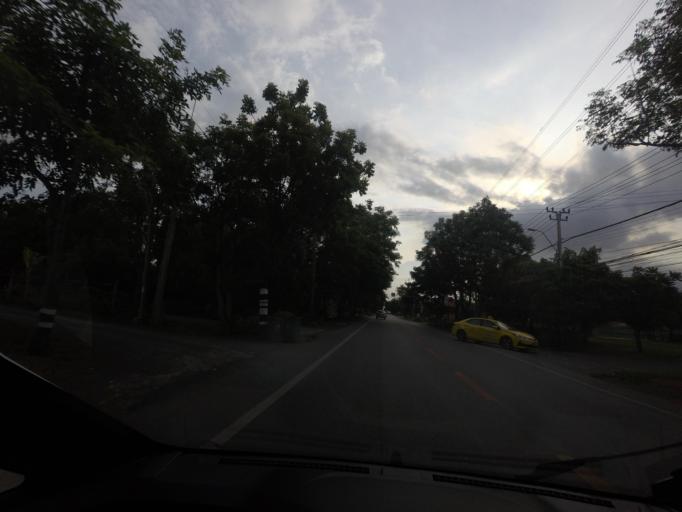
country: TH
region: Bangkok
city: Nong Chok
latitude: 13.8593
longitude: 100.8501
